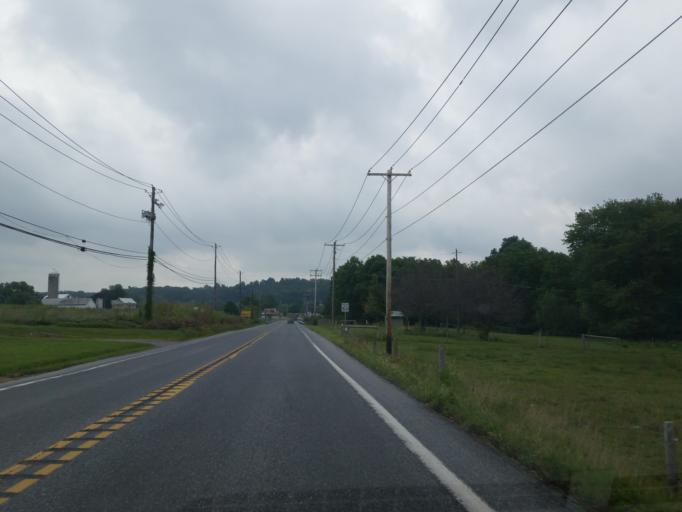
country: US
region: Pennsylvania
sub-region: Lancaster County
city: Brickerville
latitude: 40.2798
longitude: -76.3003
